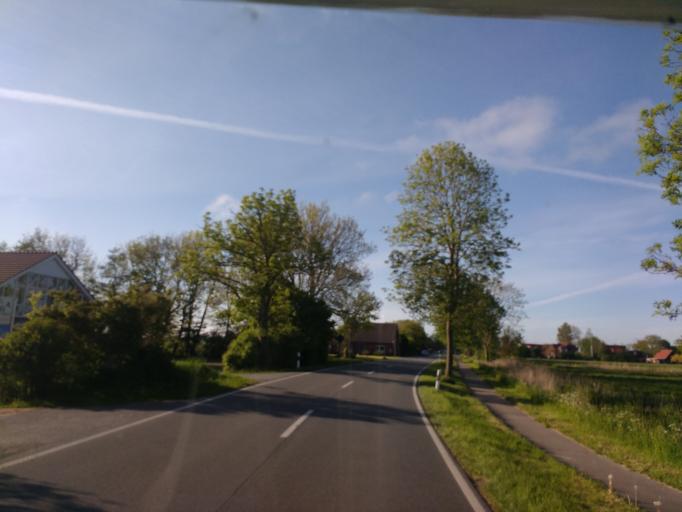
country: DE
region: Lower Saxony
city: Schillig
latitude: 53.6806
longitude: 7.9876
